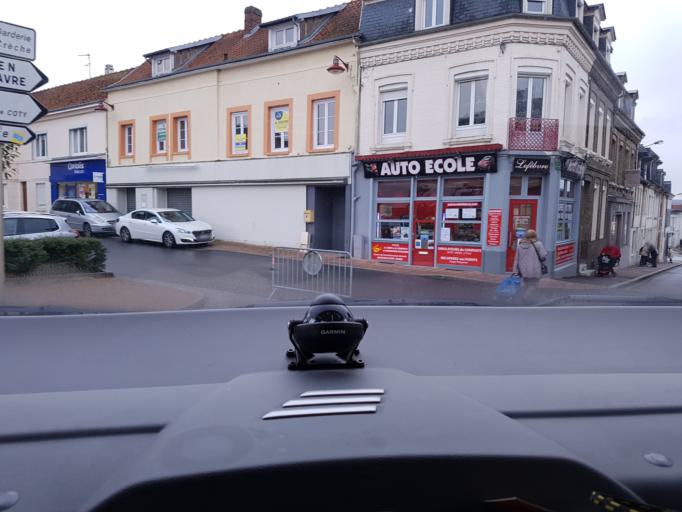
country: FR
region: Haute-Normandie
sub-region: Departement de la Seine-Maritime
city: Duclair
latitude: 49.4825
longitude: 0.8756
